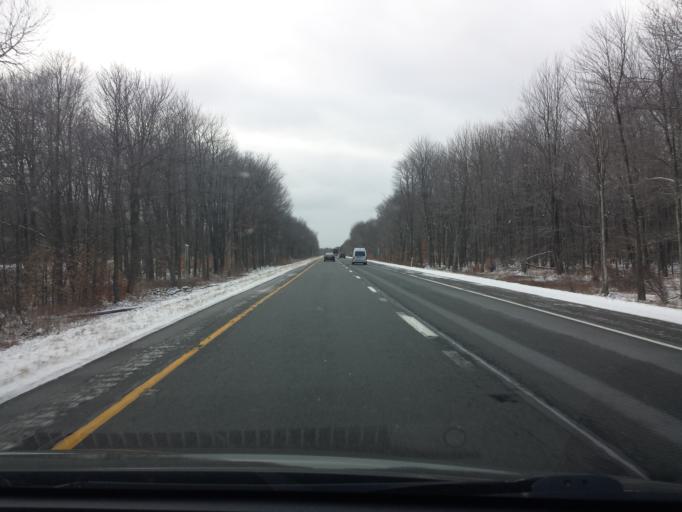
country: US
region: Pennsylvania
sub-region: Monroe County
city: Pocono Pines
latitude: 41.0733
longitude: -75.4584
